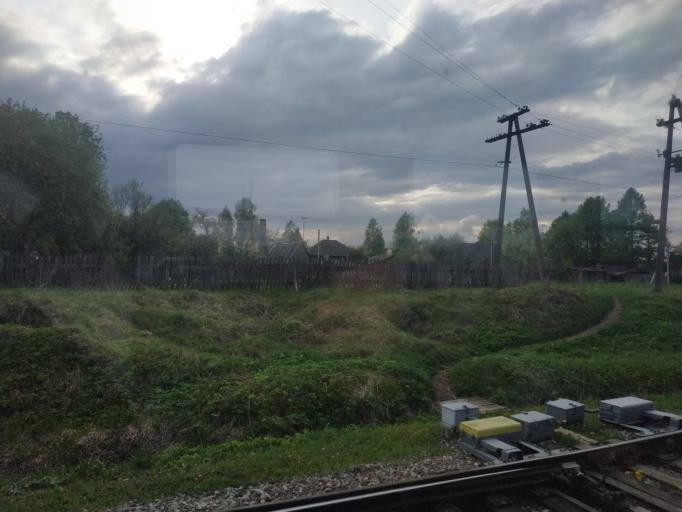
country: RU
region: Smolensk
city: Ugra
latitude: 54.7724
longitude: 34.3428
